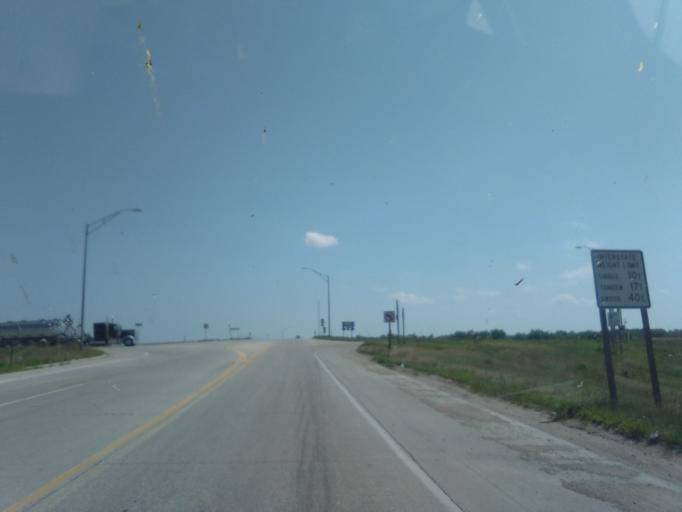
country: US
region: Nebraska
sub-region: Phelps County
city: Holdrege
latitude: 40.6923
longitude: -99.3798
